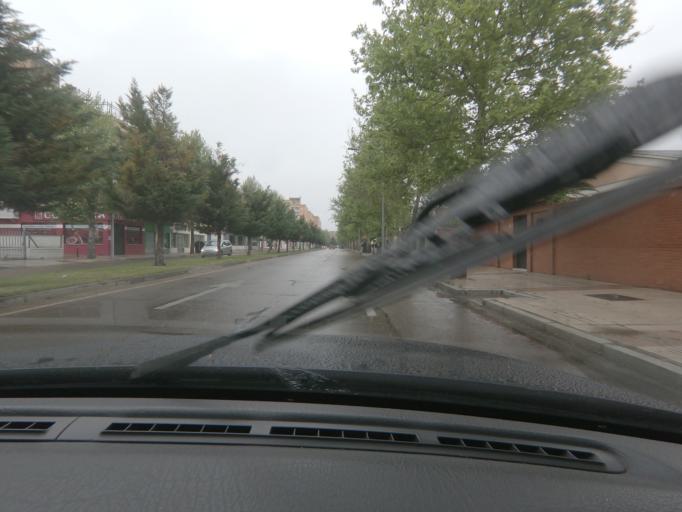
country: ES
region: Extremadura
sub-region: Provincia de Badajoz
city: Badajoz
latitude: 38.8638
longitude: -6.9725
